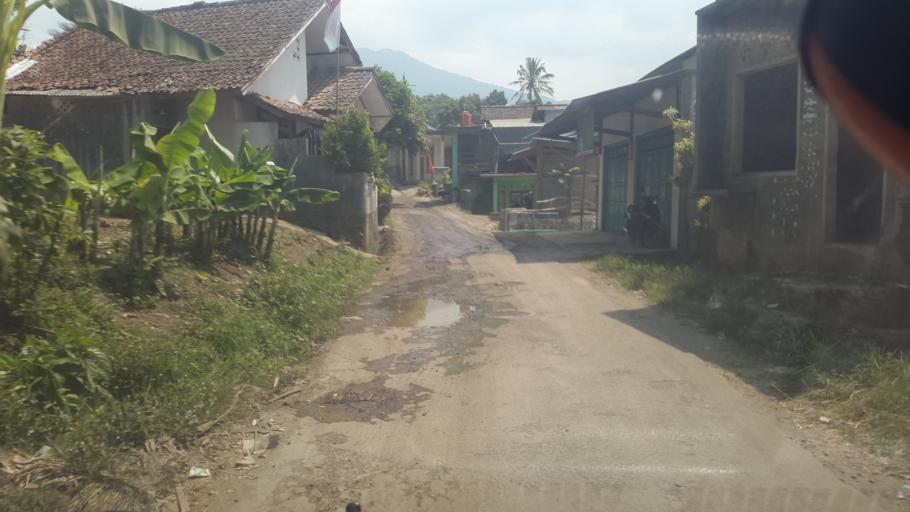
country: ID
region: West Java
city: Cicurug
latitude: -6.7806
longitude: 106.7401
